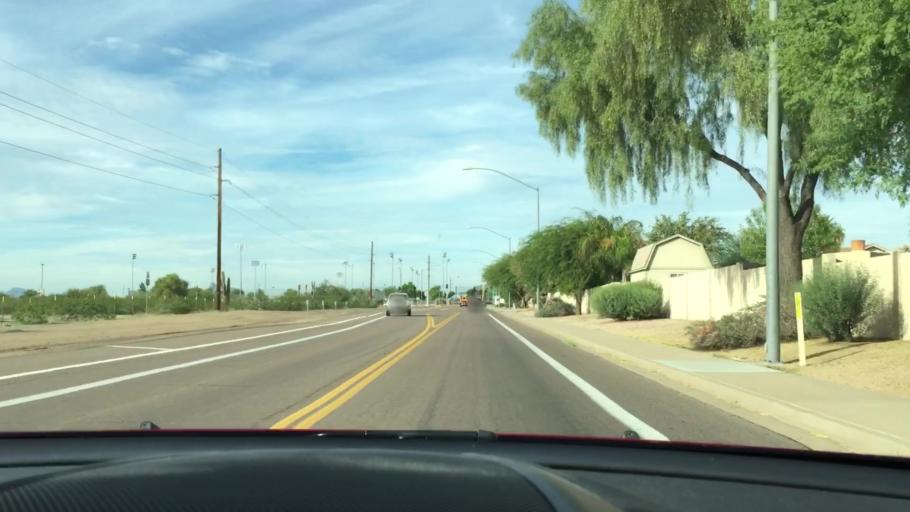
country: US
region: Arizona
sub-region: Pinal County
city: Apache Junction
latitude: 33.4343
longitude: -111.6586
